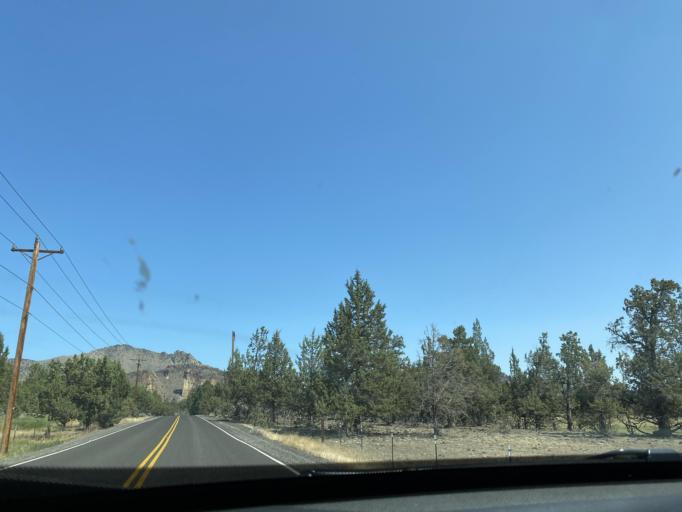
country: US
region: Oregon
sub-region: Deschutes County
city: Terrebonne
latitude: 44.3704
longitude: -121.1699
